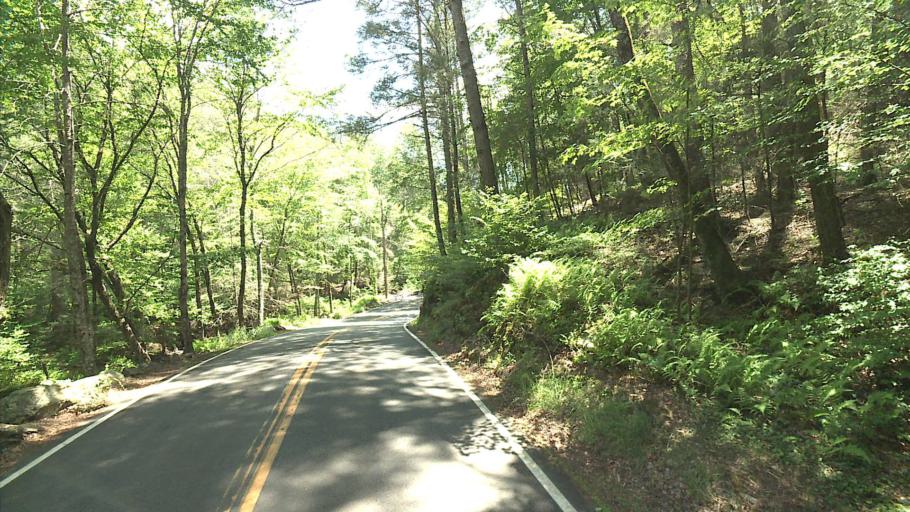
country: US
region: Connecticut
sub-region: New London County
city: Colchester
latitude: 41.4738
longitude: -72.3398
